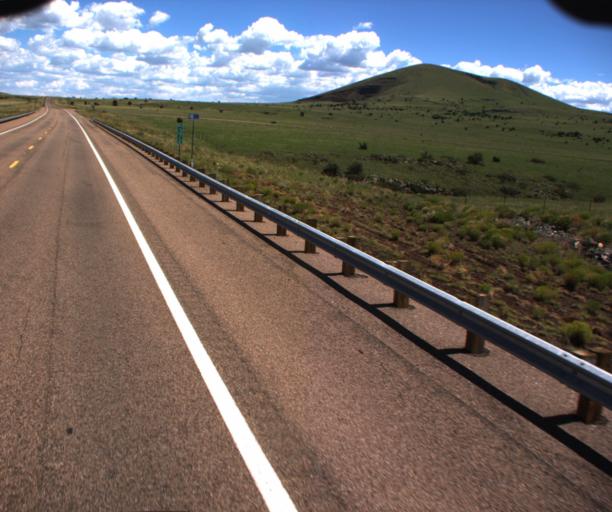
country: US
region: Arizona
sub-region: Apache County
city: Springerville
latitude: 34.2414
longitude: -109.5147
